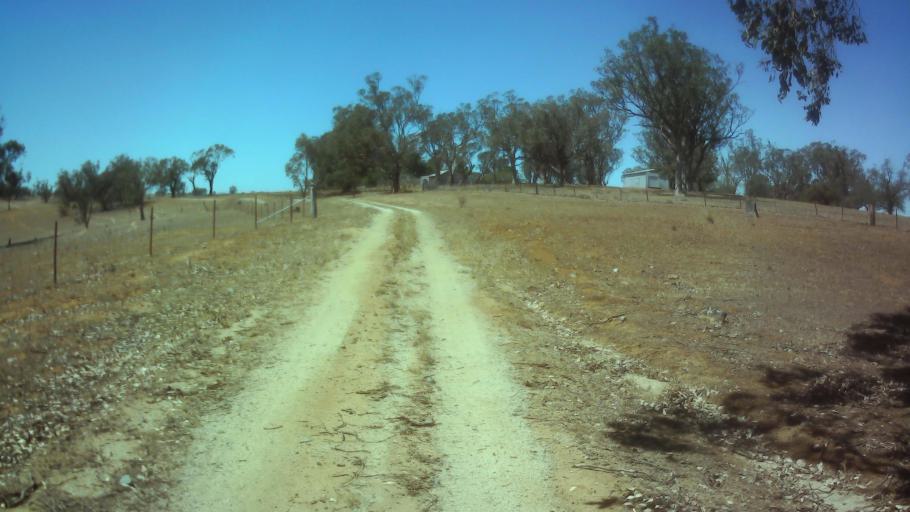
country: AU
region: New South Wales
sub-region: Cowra
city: Cowra
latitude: -33.8875
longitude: 148.4981
